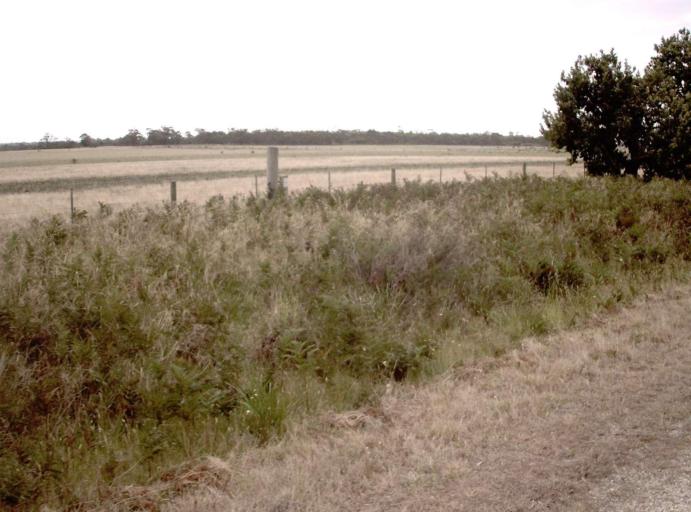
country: AU
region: Victoria
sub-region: Wellington
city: Sale
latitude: -38.1996
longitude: 147.3340
